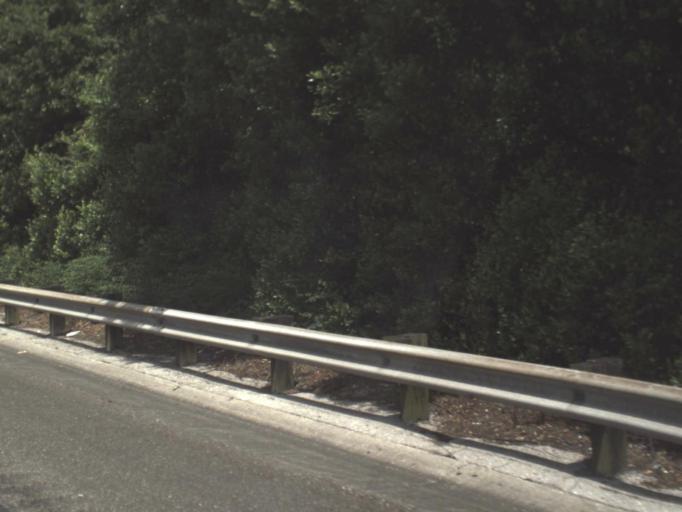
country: US
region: Florida
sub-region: Duval County
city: Jacksonville
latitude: 30.3932
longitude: -81.7573
